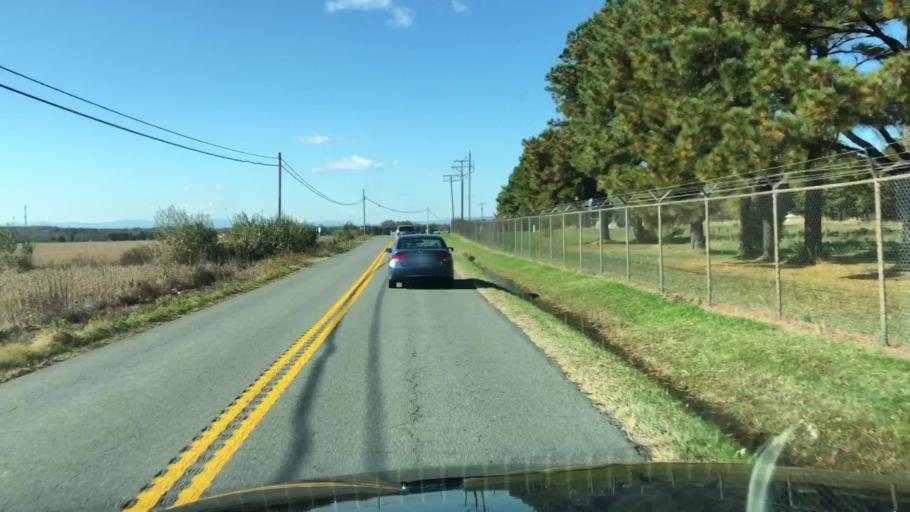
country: US
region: Virginia
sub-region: Fauquier County
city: Bealeton
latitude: 38.5144
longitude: -77.7846
